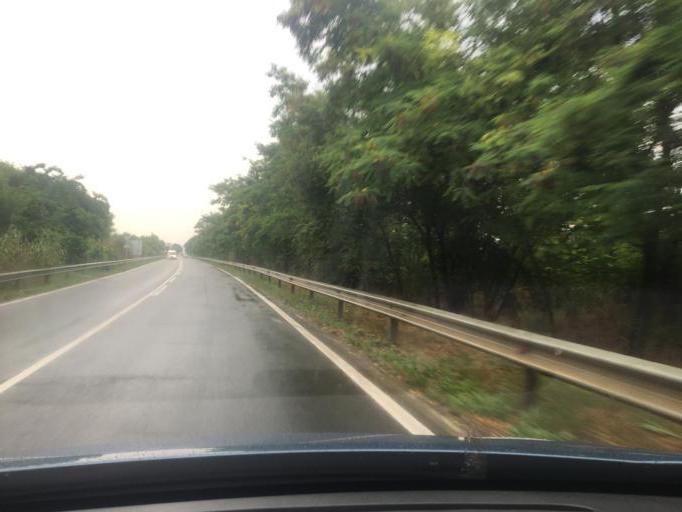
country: BG
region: Burgas
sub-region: Obshtina Pomorie
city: Pomorie
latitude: 42.5659
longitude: 27.6029
